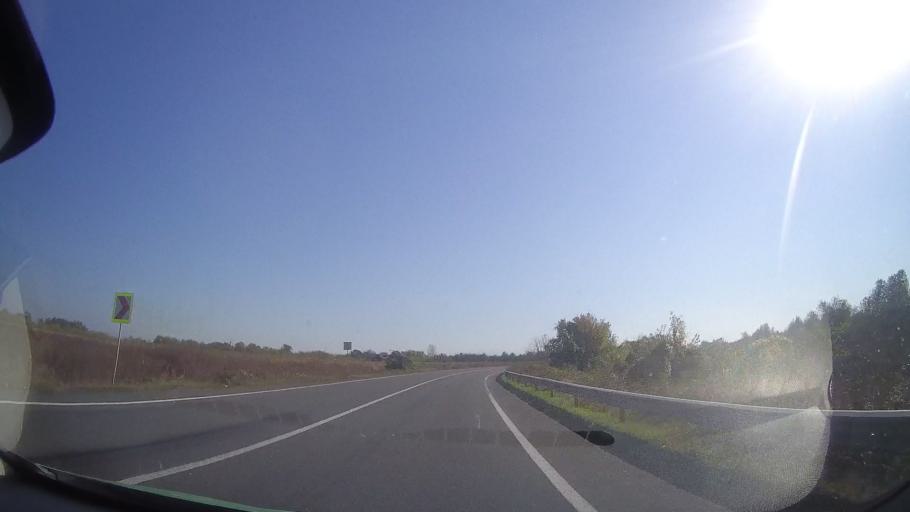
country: RO
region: Timis
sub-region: Comuna Costeiu
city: Costeiu
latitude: 45.7407
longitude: 21.8378
